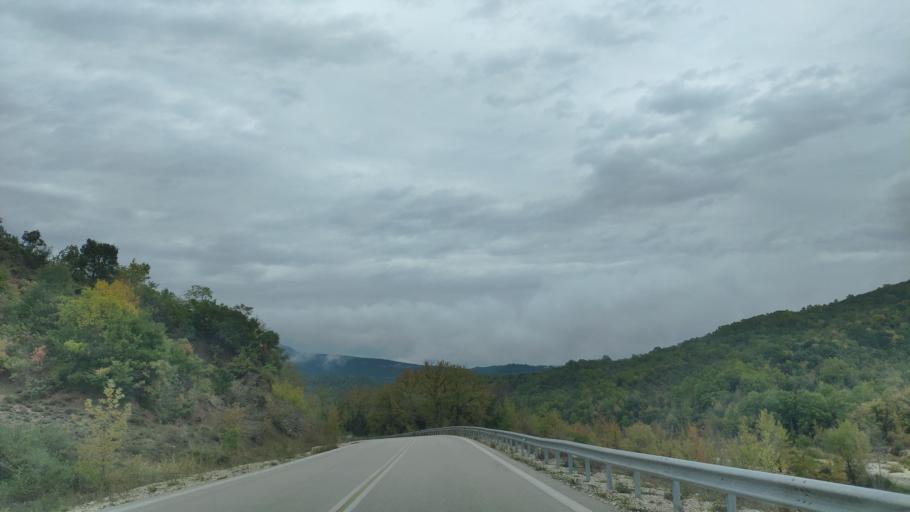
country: GR
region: Epirus
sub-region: Nomos Ioanninon
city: Pedini
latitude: 39.5261
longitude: 20.6936
